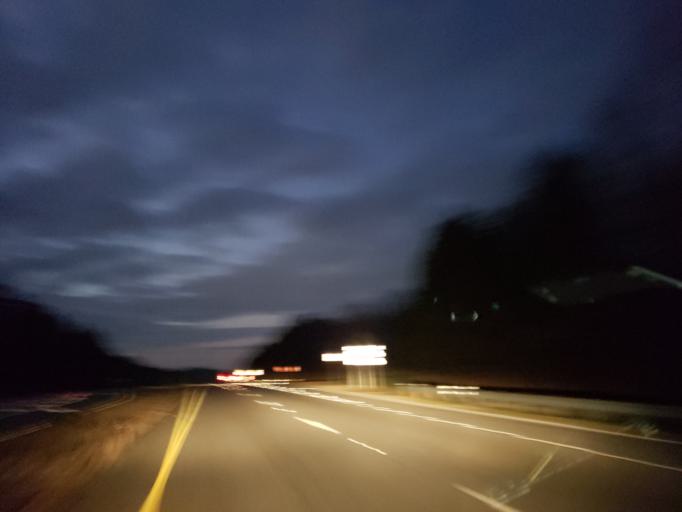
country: US
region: Georgia
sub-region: Polk County
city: Rockmart
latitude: 33.9660
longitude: -84.9942
